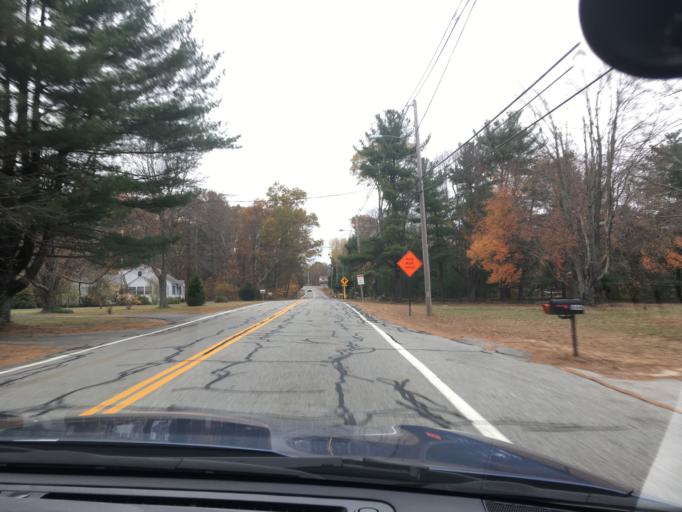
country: US
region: Rhode Island
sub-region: Providence County
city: North Scituate
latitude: 41.8095
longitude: -71.6599
